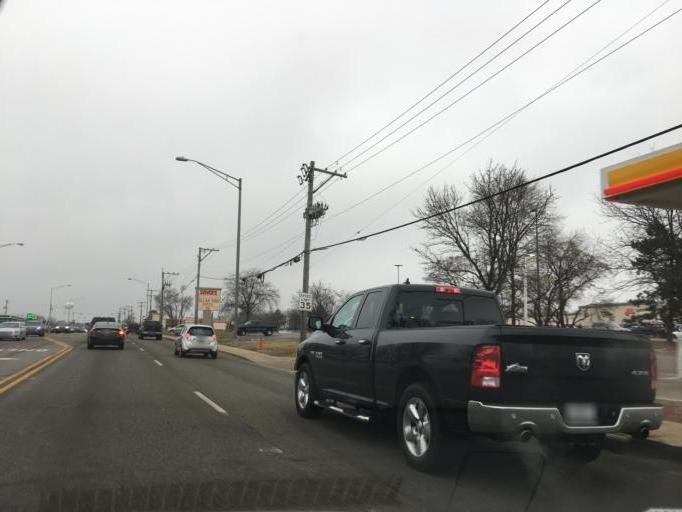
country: US
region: Illinois
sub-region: McHenry County
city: Crystal Lake
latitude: 42.2276
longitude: -88.3287
